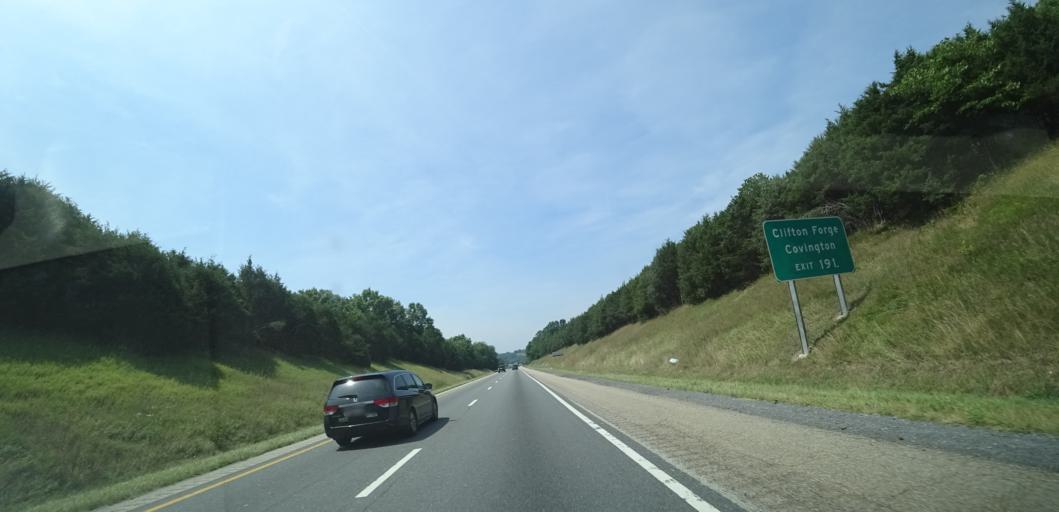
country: US
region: Virginia
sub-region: Rockbridge County
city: East Lexington
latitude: 37.8032
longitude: -79.3920
